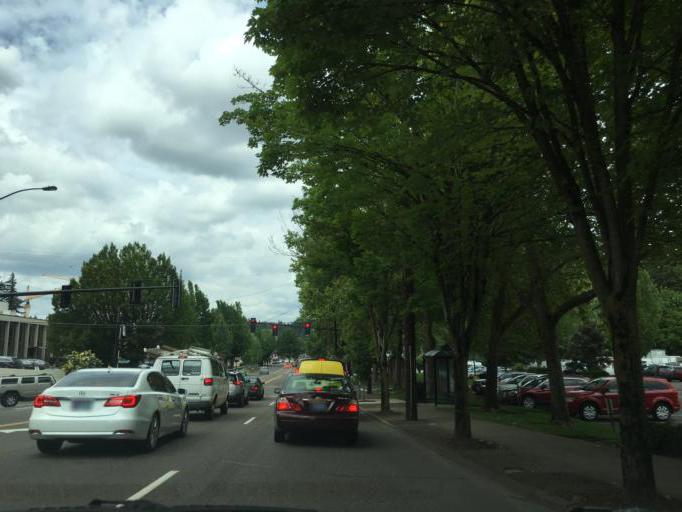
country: US
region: Oregon
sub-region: Clackamas County
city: Lake Oswego
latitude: 45.4152
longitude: -122.6638
